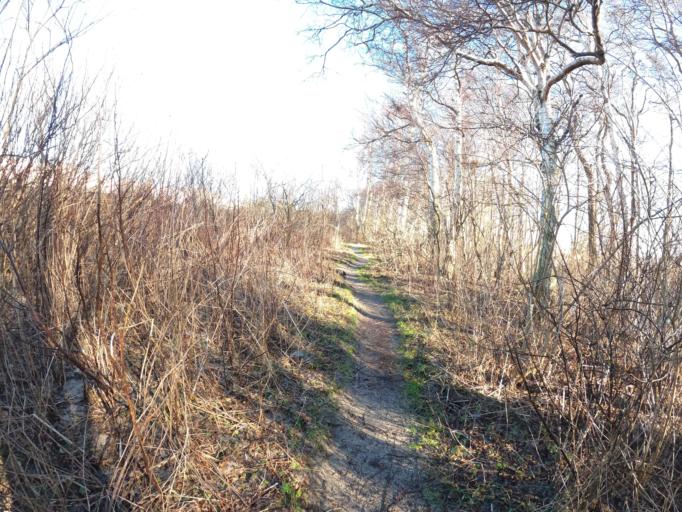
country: PL
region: West Pomeranian Voivodeship
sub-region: Powiat koszalinski
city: Sianow
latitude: 54.3366
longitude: 16.2428
